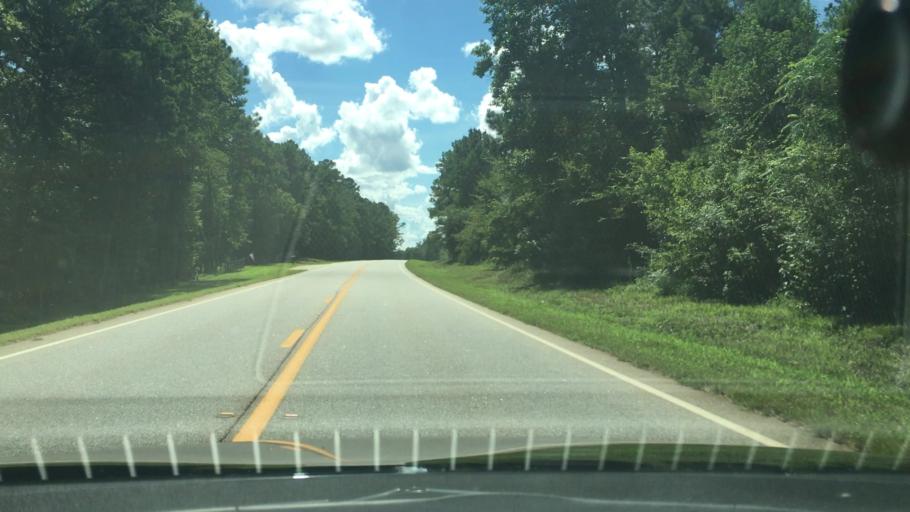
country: US
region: Georgia
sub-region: Butts County
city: Indian Springs
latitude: 33.3098
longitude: -83.8130
